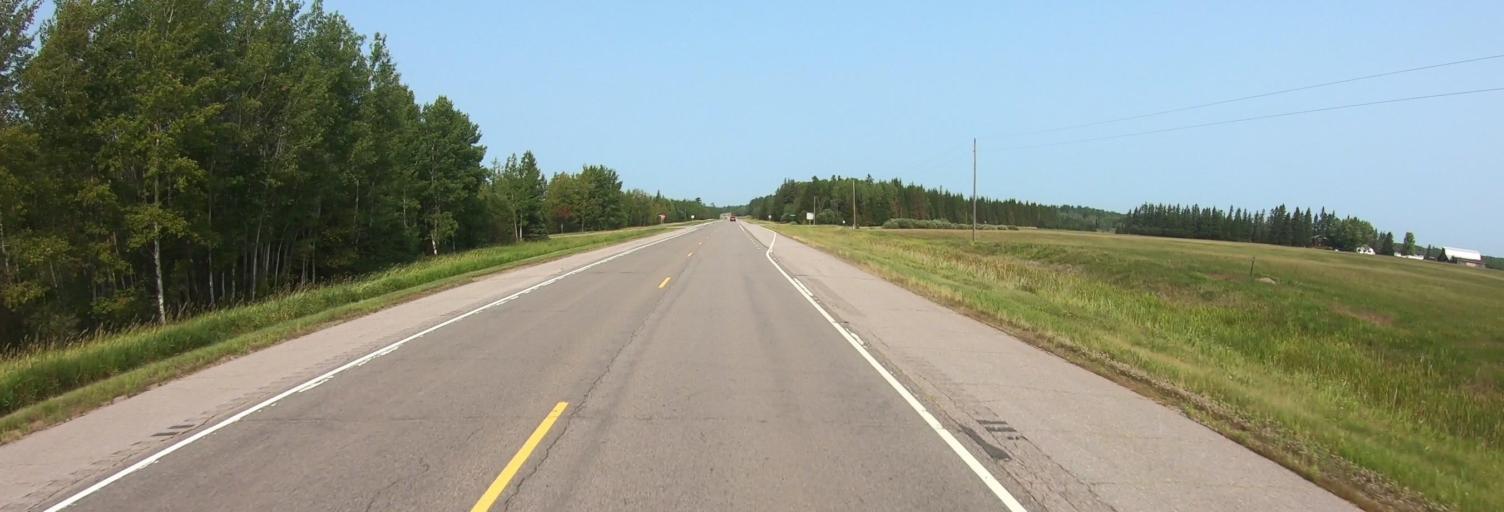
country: US
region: Minnesota
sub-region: Saint Louis County
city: Mountain Iron
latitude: 47.8779
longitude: -92.7602
